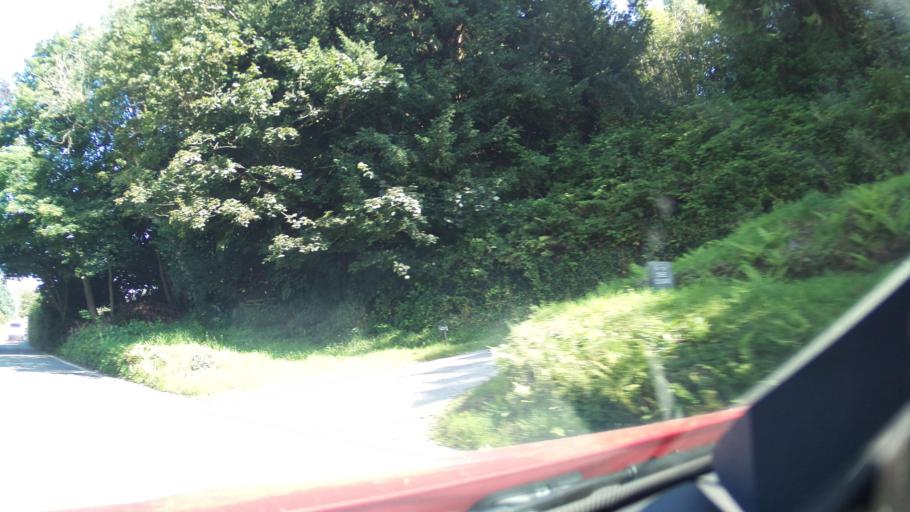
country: GB
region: England
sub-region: Devon
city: Tavistock
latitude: 50.5521
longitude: -4.1341
